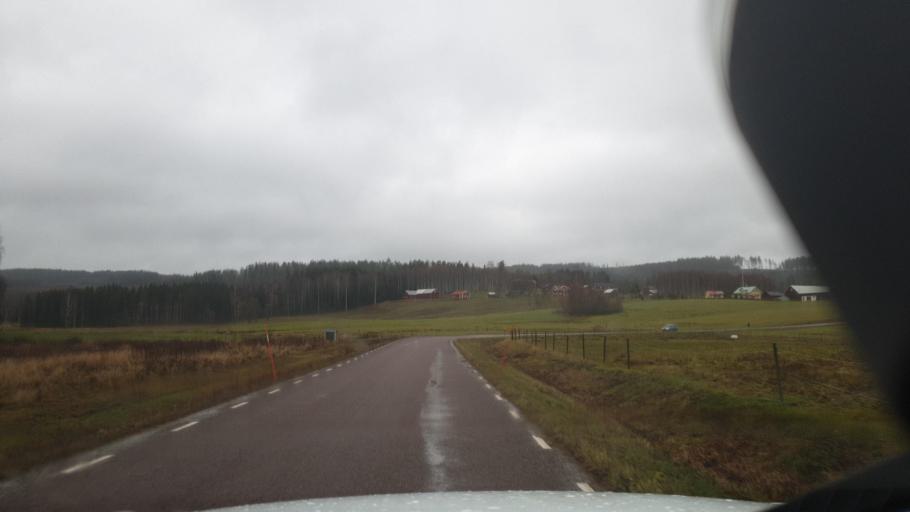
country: SE
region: Vaermland
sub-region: Sunne Kommun
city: Sunne
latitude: 59.7419
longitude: 13.0720
